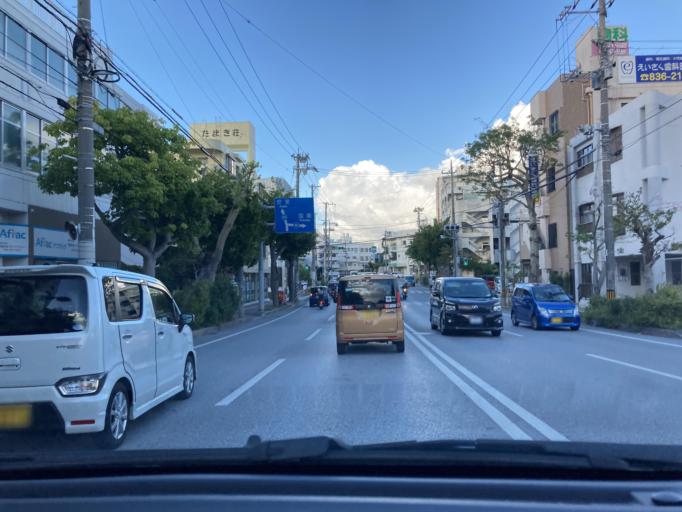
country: JP
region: Okinawa
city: Naha-shi
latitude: 26.2033
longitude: 127.6984
